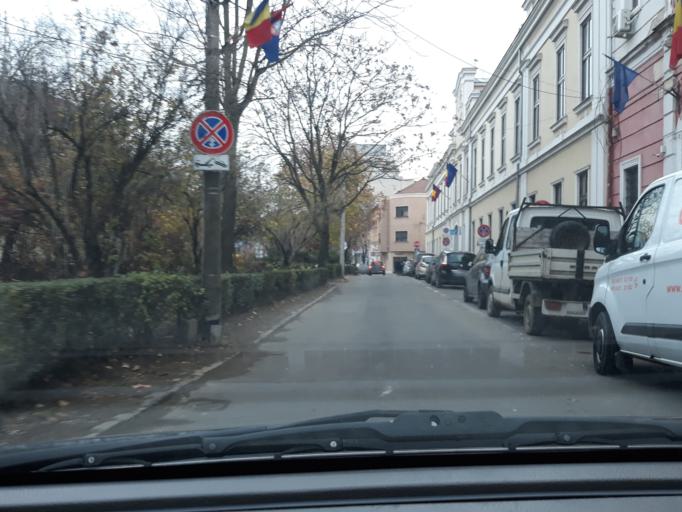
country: RO
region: Bihor
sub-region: Comuna Biharea
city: Oradea
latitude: 47.0580
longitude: 21.9345
